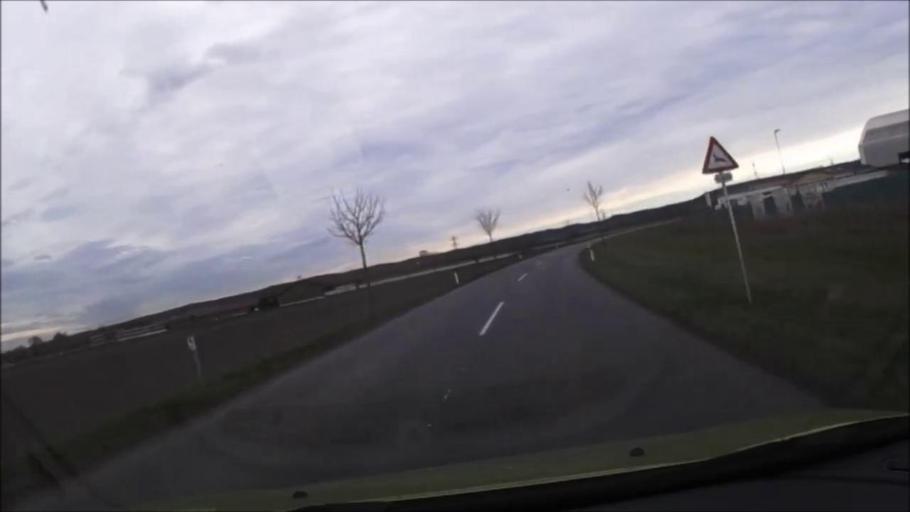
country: AT
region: Burgenland
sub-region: Eisenstadt-Umgebung
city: Leithaprodersdorf
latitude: 47.9341
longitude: 16.4912
